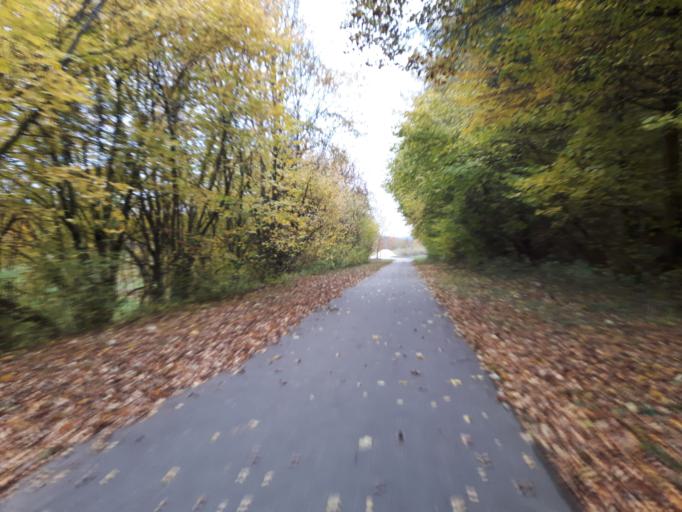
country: DE
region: Baden-Wuerttemberg
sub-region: Karlsruhe Region
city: Zaisenhausen
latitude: 49.1686
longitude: 8.7728
